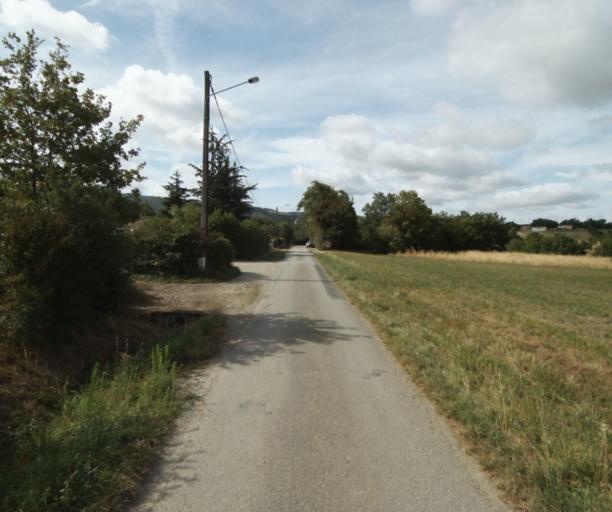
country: FR
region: Midi-Pyrenees
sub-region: Departement du Tarn
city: Soreze
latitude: 43.4742
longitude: 2.0849
